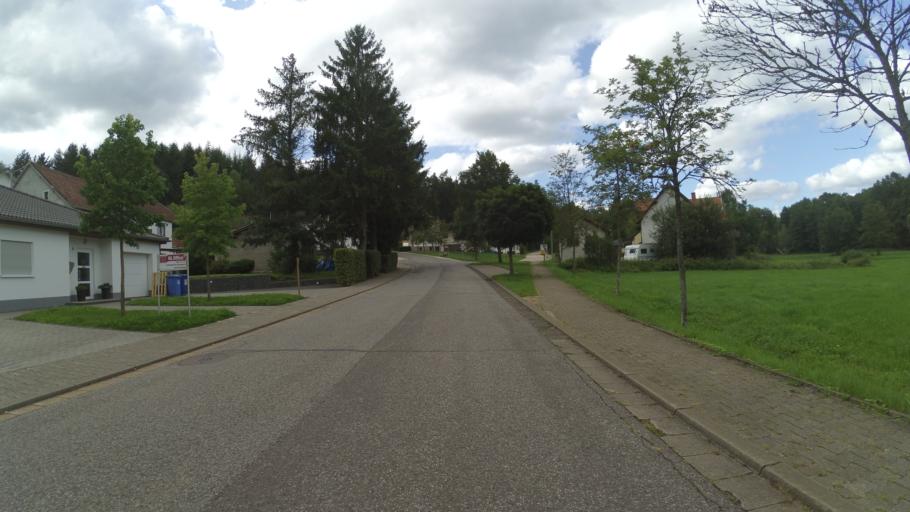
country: DE
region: Saarland
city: Nonnweiler
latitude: 49.5847
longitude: 6.9893
